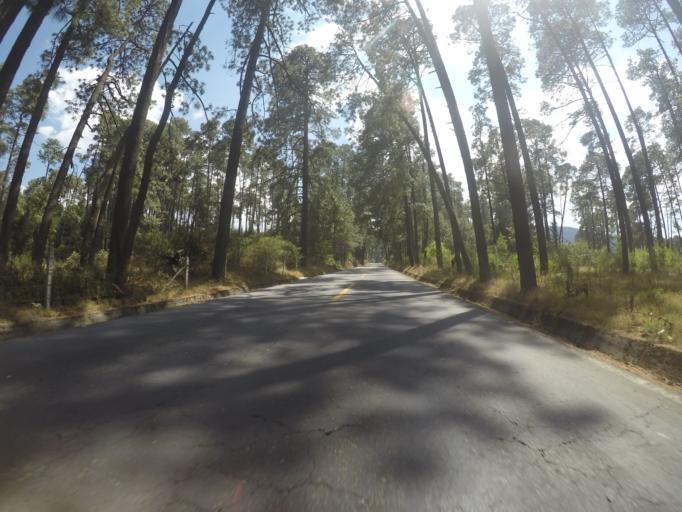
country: MX
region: Mexico
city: Cerro La Calera
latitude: 19.2060
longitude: -99.8095
